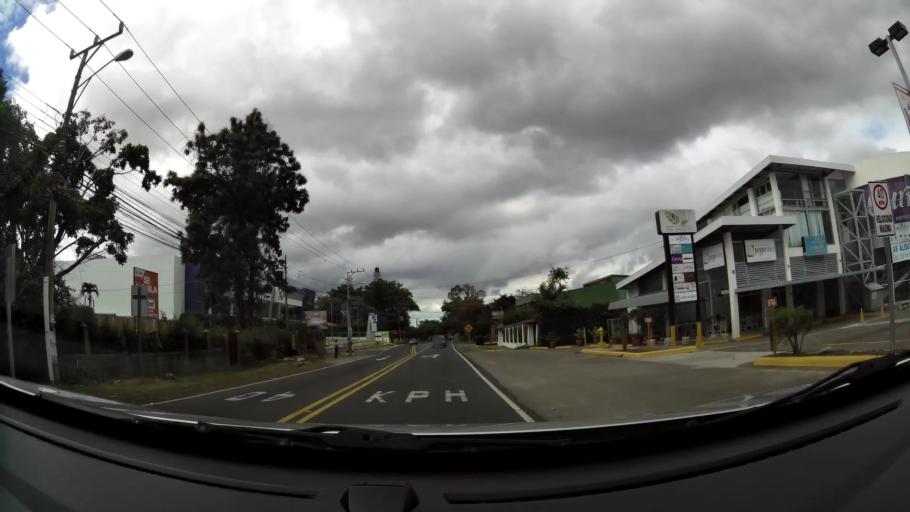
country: CR
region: Cartago
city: San Diego
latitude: 9.9102
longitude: -84.0123
